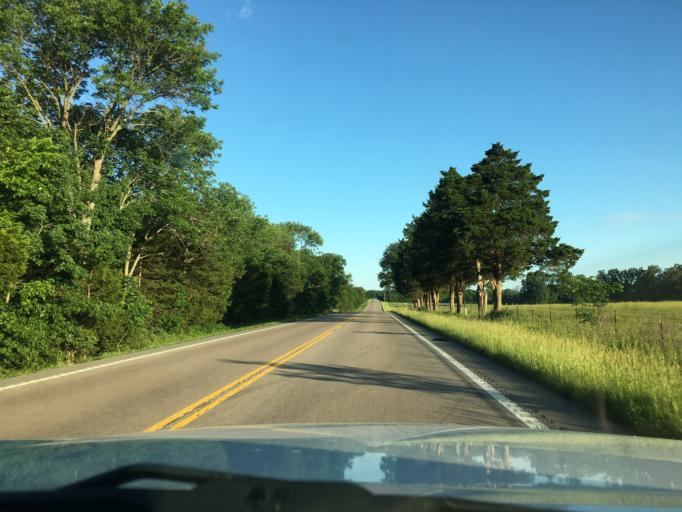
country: US
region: Missouri
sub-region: Gasconade County
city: Owensville
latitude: 38.4520
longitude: -91.4512
